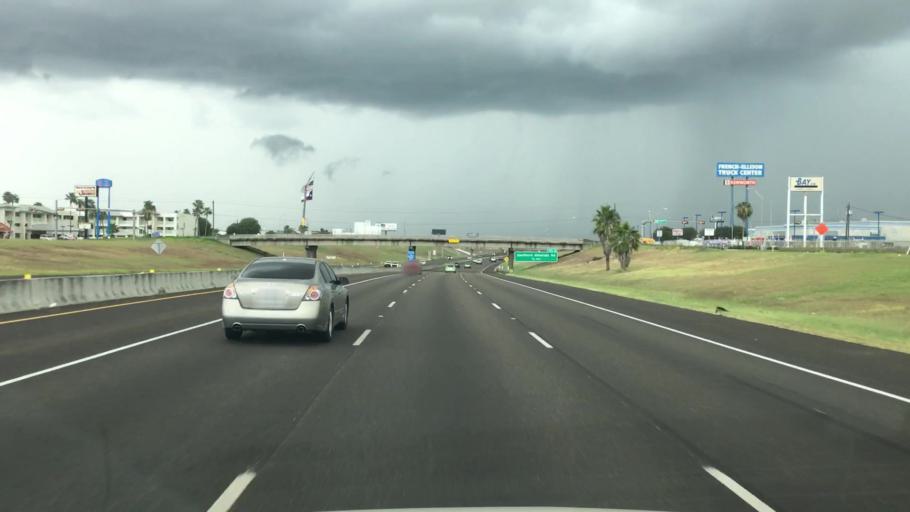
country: US
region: Texas
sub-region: Nueces County
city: Corpus Christi
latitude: 27.8050
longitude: -97.4827
